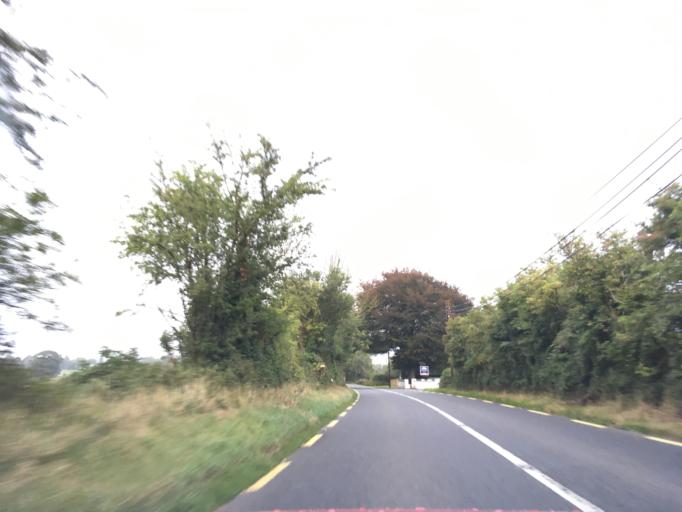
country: IE
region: Munster
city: Cashel
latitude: 52.4949
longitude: -8.0112
